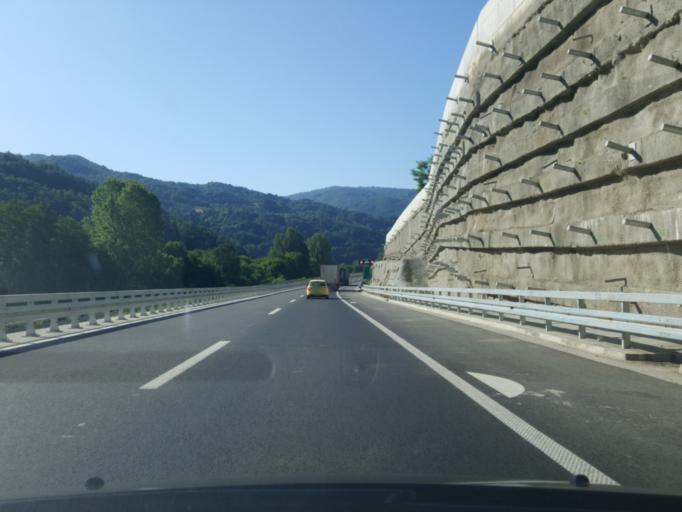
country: RS
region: Central Serbia
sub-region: Jablanicki Okrug
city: Vlasotince
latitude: 42.8516
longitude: 22.1273
